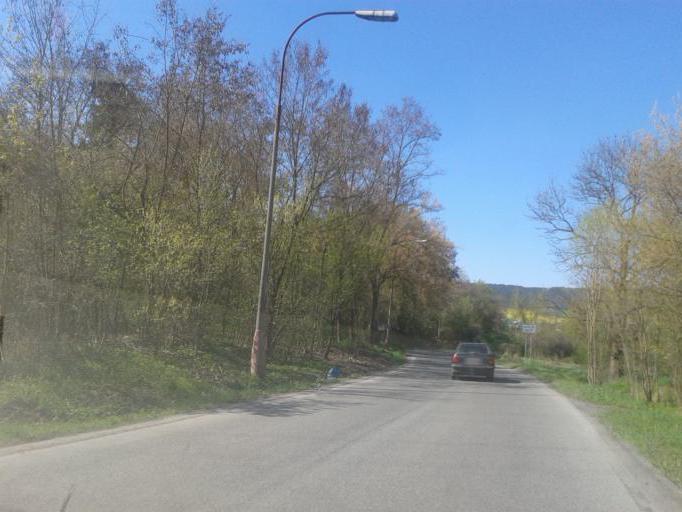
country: CZ
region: Central Bohemia
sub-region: Okres Beroun
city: Kraluv Dvur
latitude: 49.9407
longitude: 14.0448
